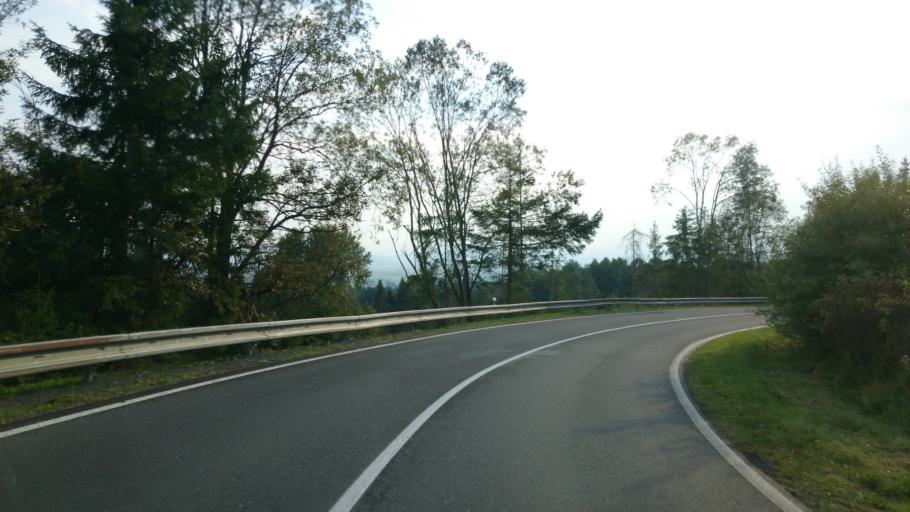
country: SK
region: Presovsky
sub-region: Okres Poprad
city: Strba
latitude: 49.0975
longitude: 20.0693
